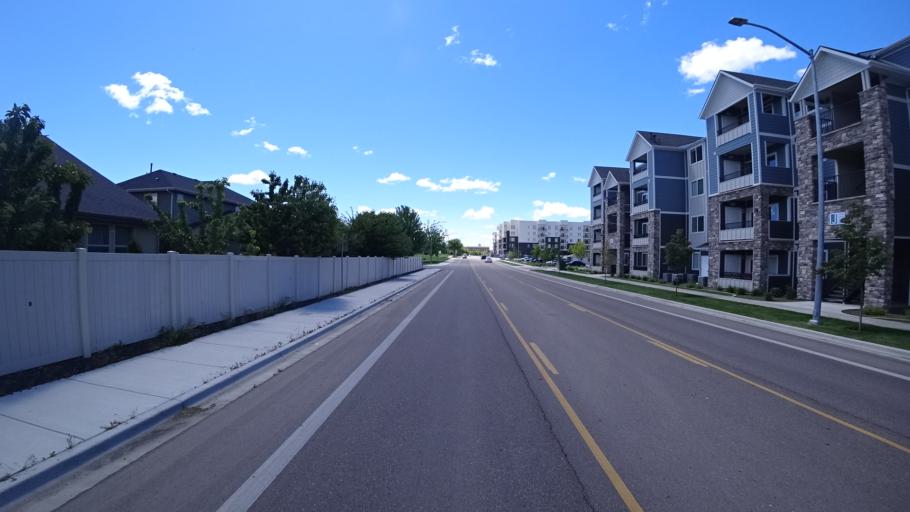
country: US
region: Idaho
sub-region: Ada County
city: Meridian
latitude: 43.6280
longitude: -116.3496
